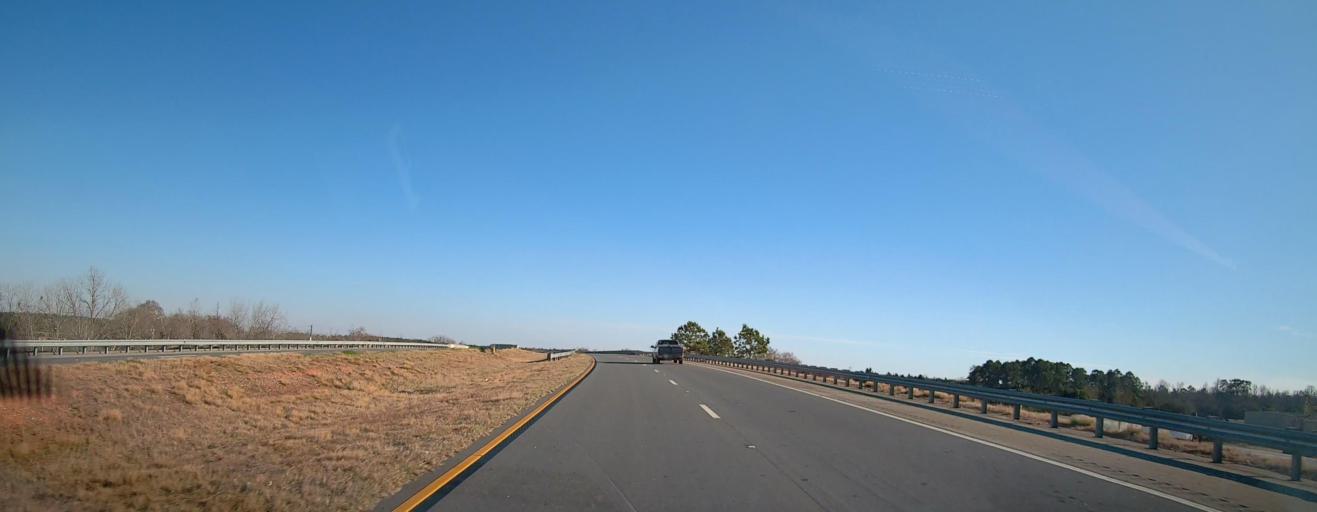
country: US
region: Georgia
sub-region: Sumter County
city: Americus
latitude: 31.8971
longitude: -84.2615
